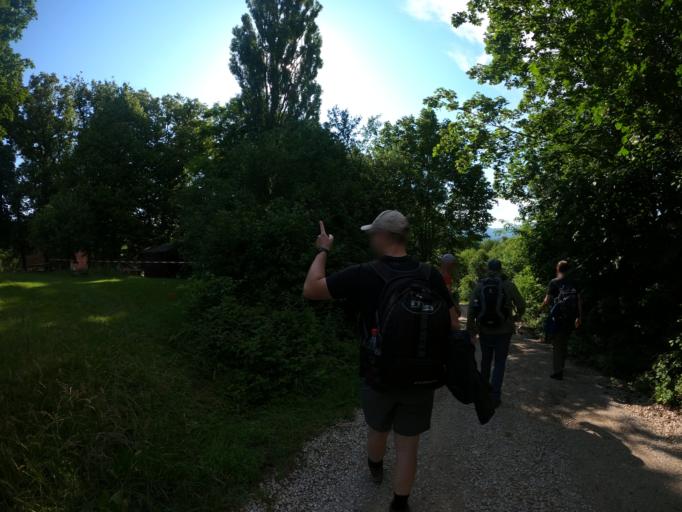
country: DE
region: Bavaria
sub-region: Upper Franconia
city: Litzendorf
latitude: 49.8772
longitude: 11.0101
